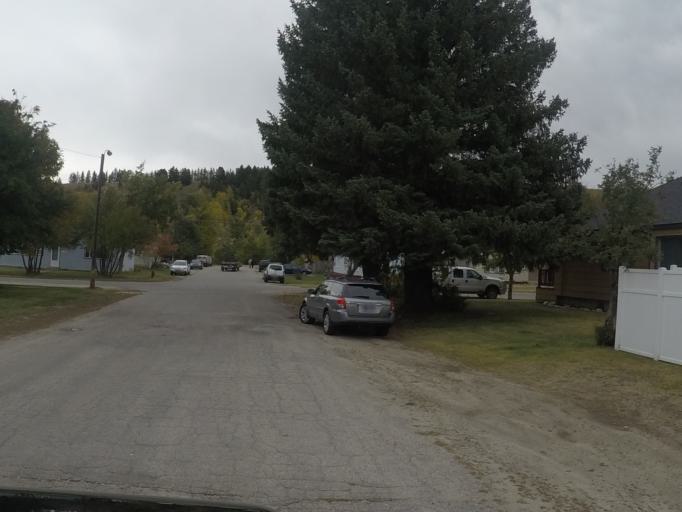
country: US
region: Montana
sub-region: Carbon County
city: Red Lodge
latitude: 45.1889
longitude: -109.2450
